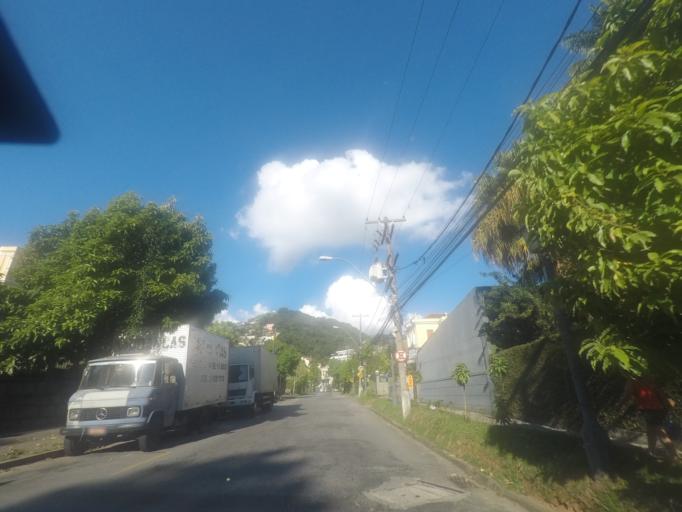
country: BR
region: Rio de Janeiro
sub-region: Petropolis
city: Petropolis
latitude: -22.5080
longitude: -43.1679
